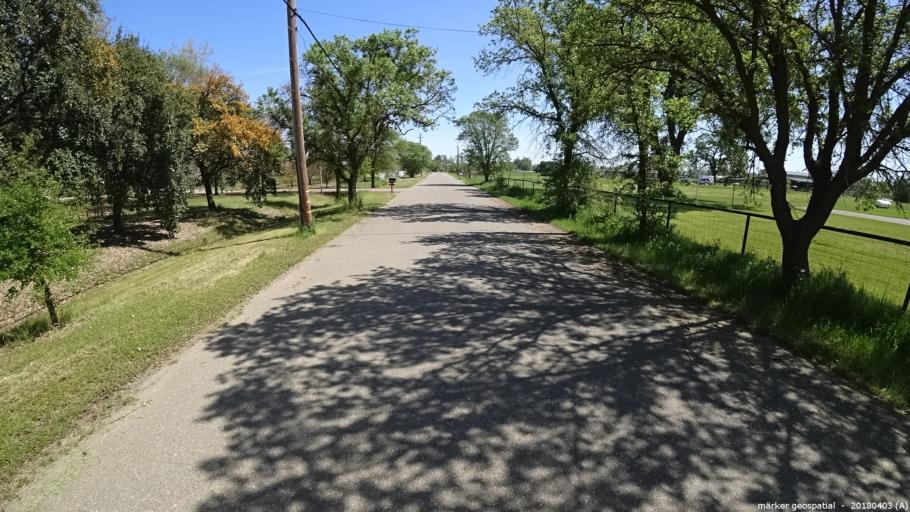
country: US
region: California
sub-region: Sacramento County
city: Wilton
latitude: 38.3942
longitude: -121.2546
